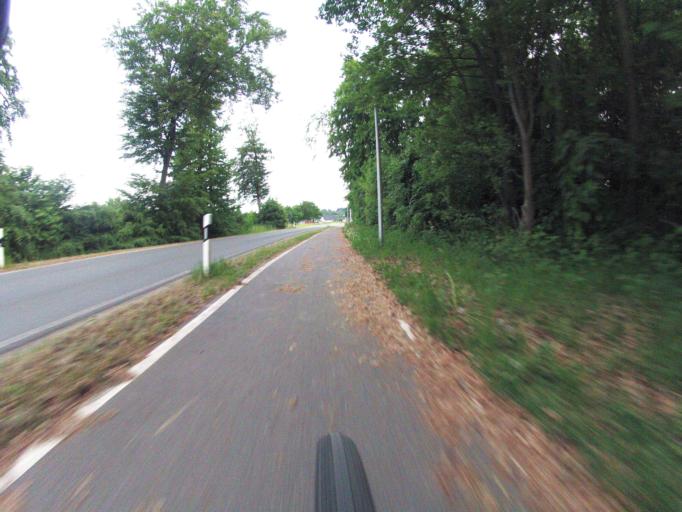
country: DE
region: North Rhine-Westphalia
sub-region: Regierungsbezirk Munster
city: Mettingen
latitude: 52.2690
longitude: 7.7983
